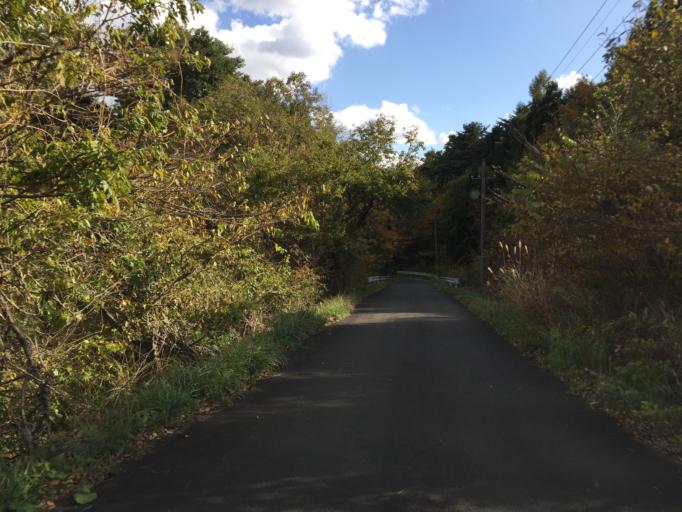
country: JP
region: Fukushima
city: Fukushima-shi
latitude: 37.7149
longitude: 140.3152
